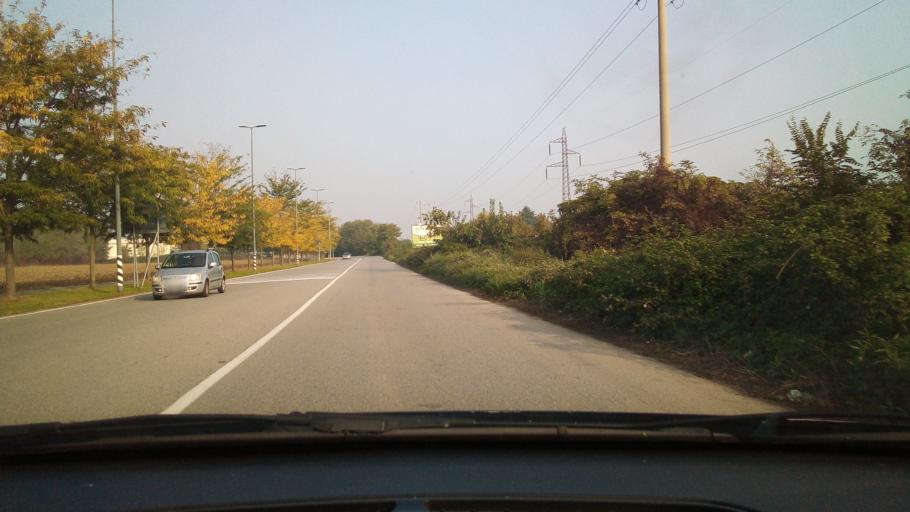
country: IT
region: Lombardy
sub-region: Citta metropolitana di Milano
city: Novegro-Tregarezzo-San Felice
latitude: 45.4811
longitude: 9.2649
